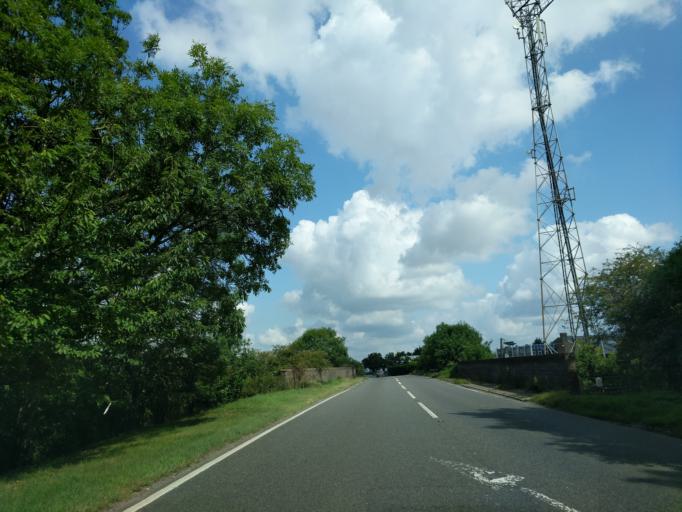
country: GB
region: England
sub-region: Suffolk
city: Exning
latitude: 52.2834
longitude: 0.3933
